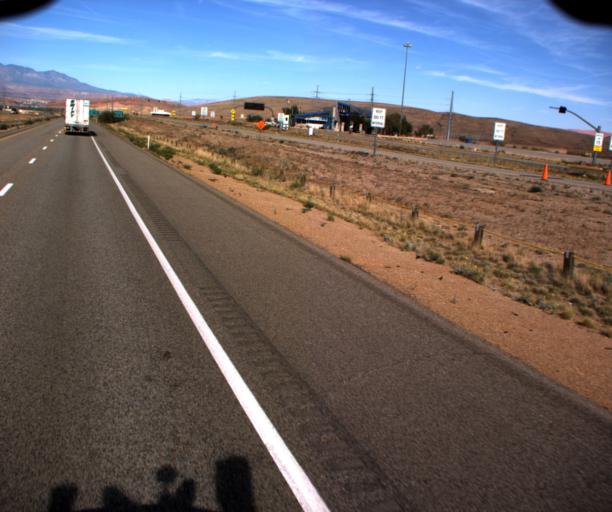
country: US
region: Utah
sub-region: Washington County
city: Saint George
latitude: 37.0117
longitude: -113.6151
